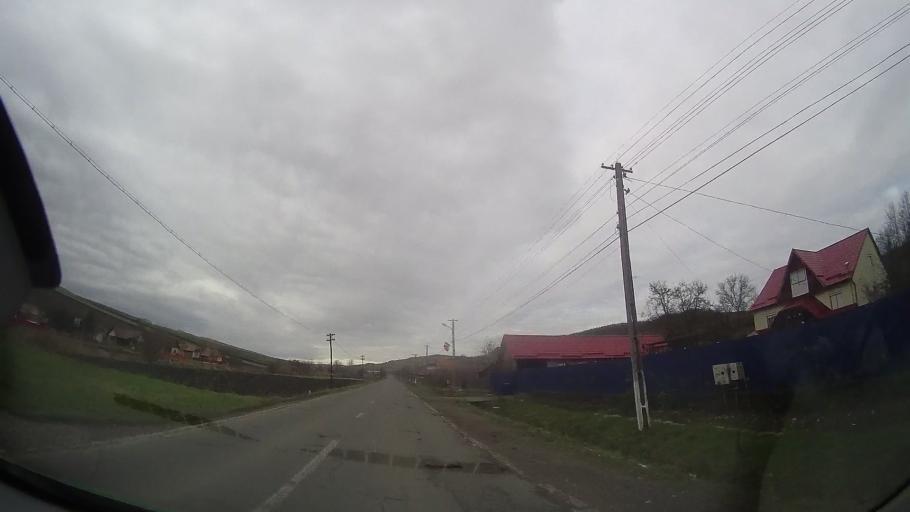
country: RO
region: Mures
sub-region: Comuna Craesti
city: Craiesti
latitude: 46.7559
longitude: 24.4183
